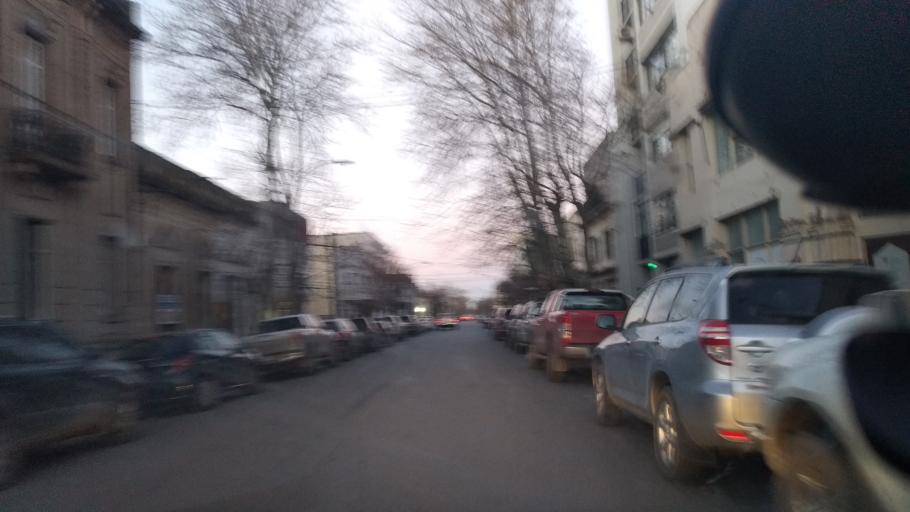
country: AR
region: Buenos Aires
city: Necochea
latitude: -38.5520
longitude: -58.7401
